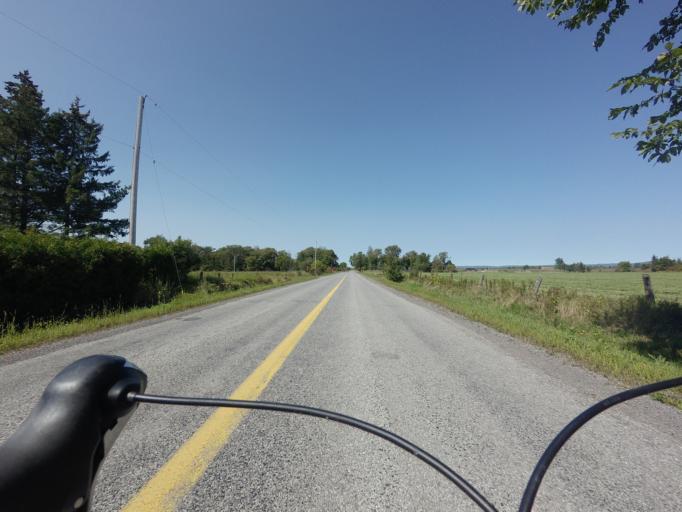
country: CA
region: Ontario
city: Bells Corners
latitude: 45.4382
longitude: -76.0678
